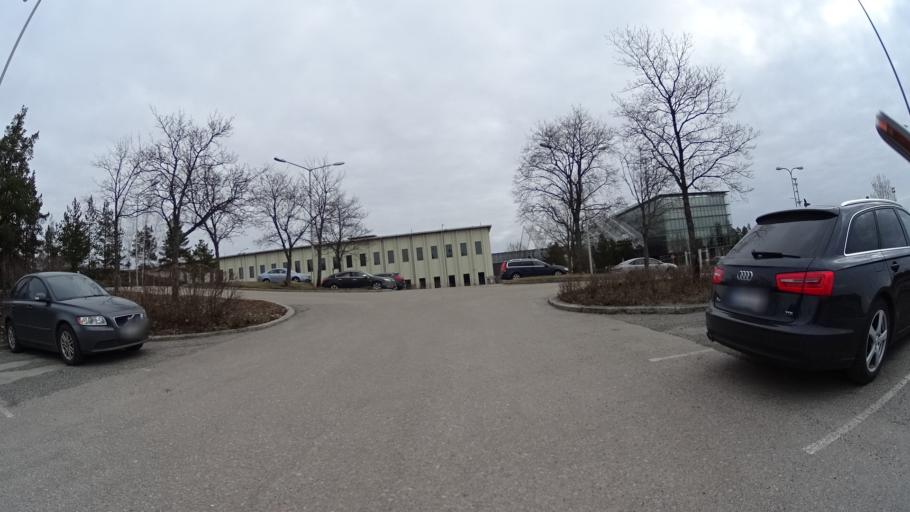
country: FI
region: Uusimaa
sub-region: Helsinki
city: Teekkarikylae
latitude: 60.3018
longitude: 24.8882
